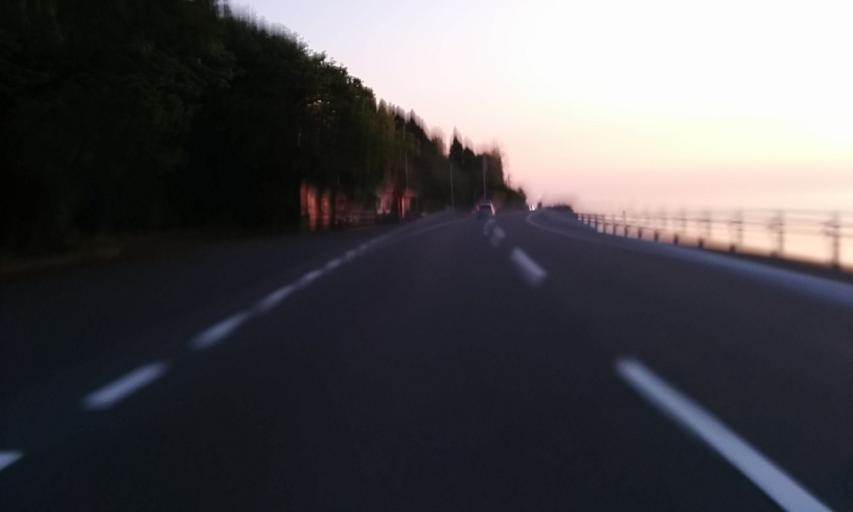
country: JP
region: Ehime
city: Ozu
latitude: 33.6448
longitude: 132.5548
